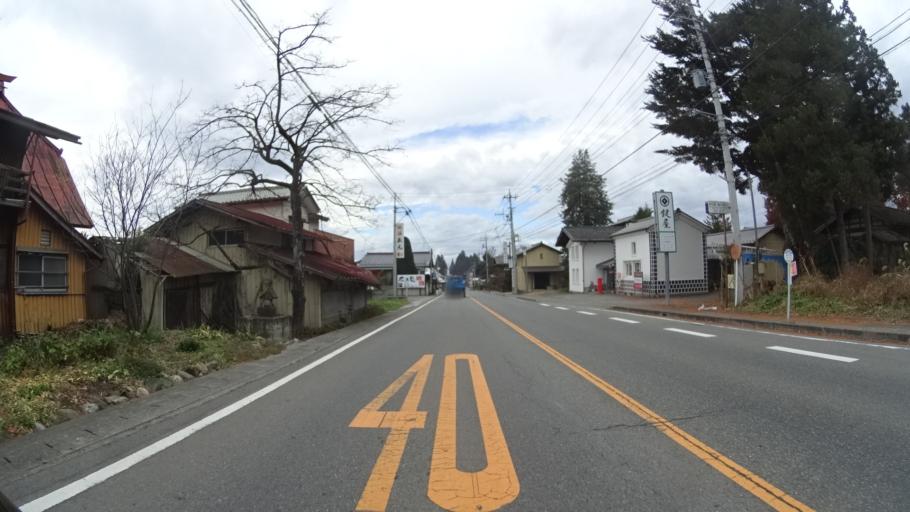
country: JP
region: Gunma
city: Numata
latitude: 36.6635
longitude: 139.1410
